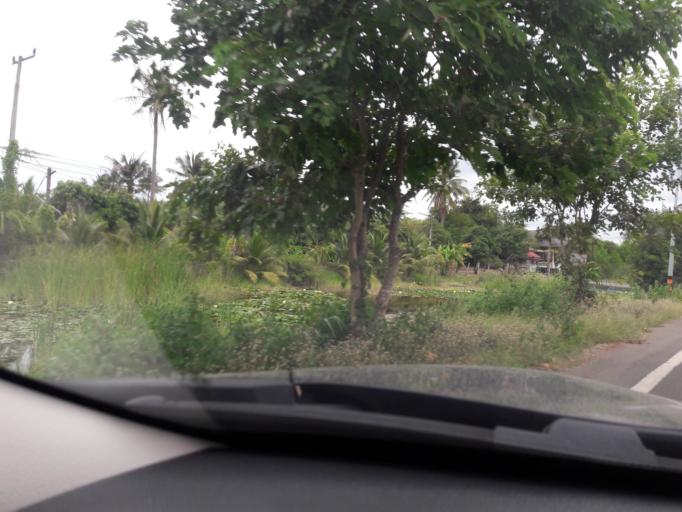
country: TH
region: Ratchaburi
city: Damnoen Saduak
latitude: 13.6021
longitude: 99.9422
